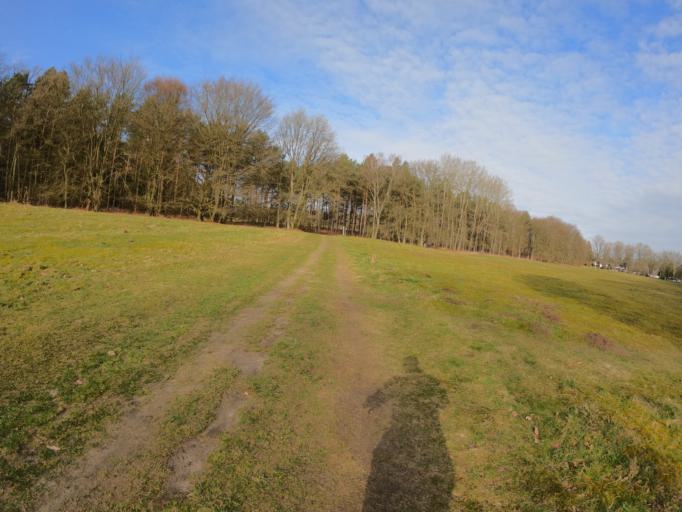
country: DE
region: Lower Saxony
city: Neu Wulmstorf
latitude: 53.4468
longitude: 9.8689
